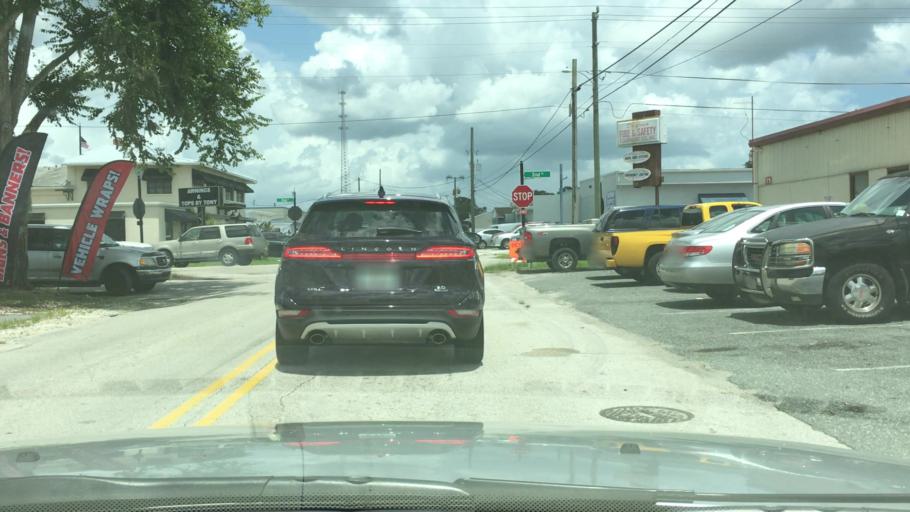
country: US
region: Florida
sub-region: Volusia County
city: Holly Hill
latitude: 29.2280
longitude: -81.0341
